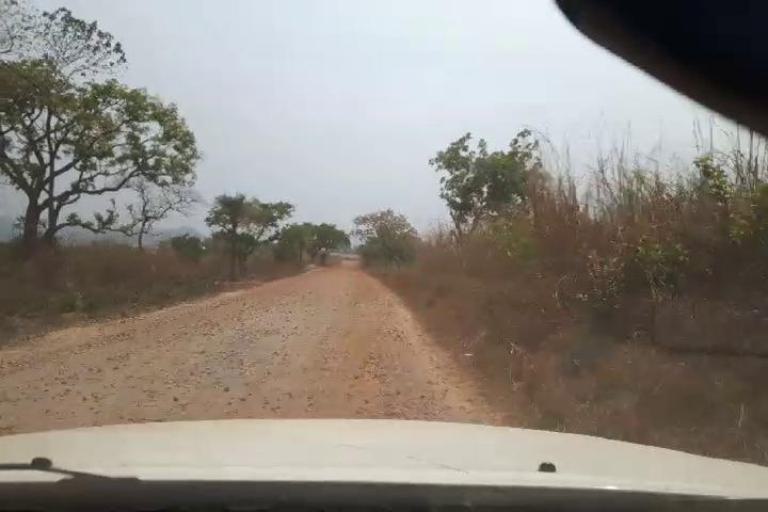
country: SL
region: Northern Province
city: Bumbuna
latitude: 9.0081
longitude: -11.7725
